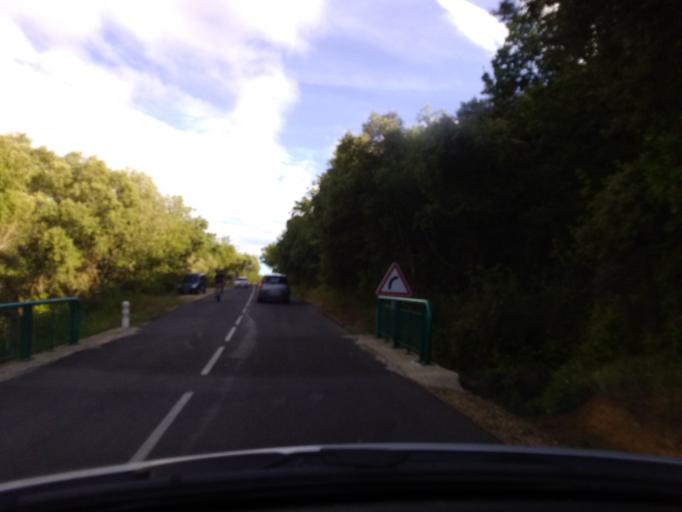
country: FR
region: Languedoc-Roussillon
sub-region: Departement de l'Herault
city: Saint-Andre-de-Sangonis
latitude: 43.6689
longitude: 3.5223
